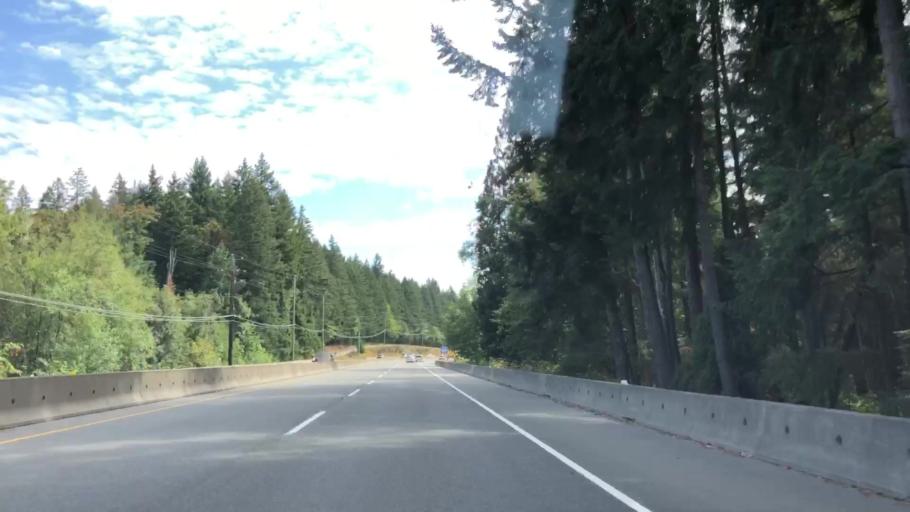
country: CA
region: British Columbia
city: North Cowichan
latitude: 48.8898
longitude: -123.7071
